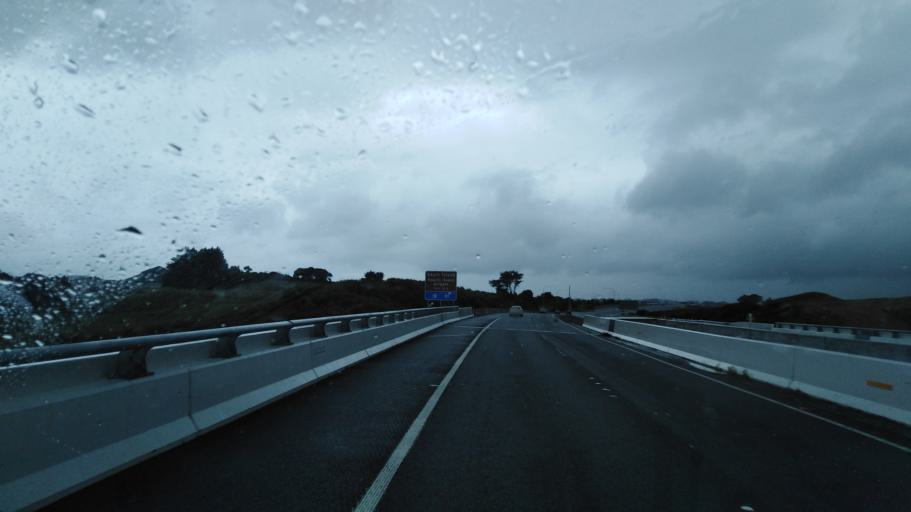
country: NZ
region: Wellington
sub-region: Kapiti Coast District
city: Paraparaumu
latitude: -40.9155
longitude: 174.9925
